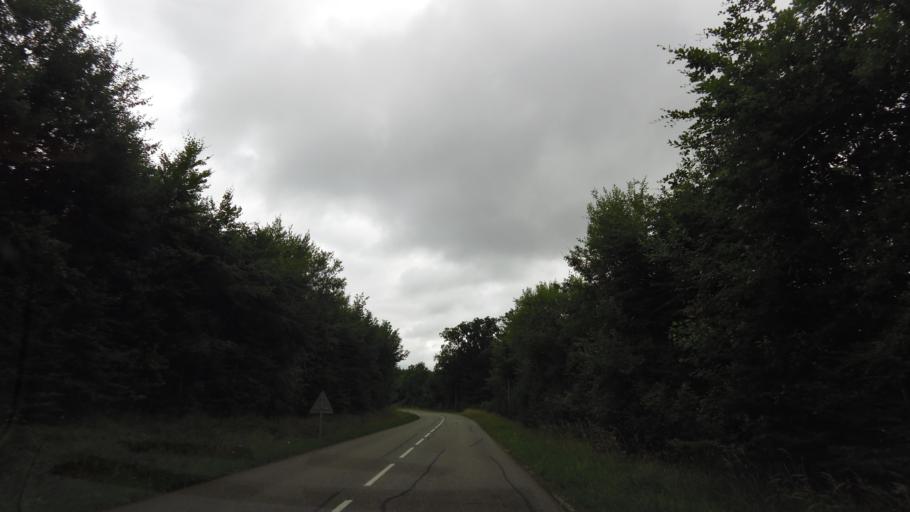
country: FR
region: Lorraine
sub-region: Departement de la Moselle
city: Lorquin
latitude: 48.6447
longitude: 6.9358
